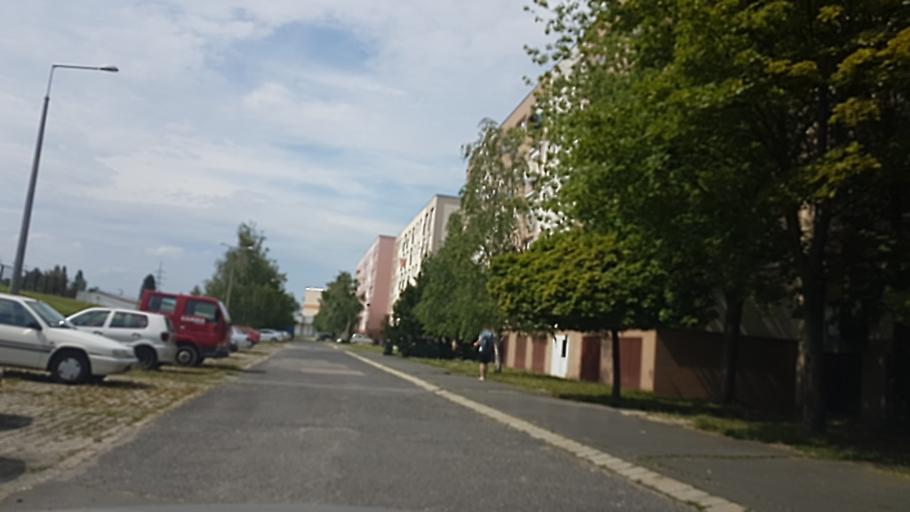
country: HU
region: Gyor-Moson-Sopron
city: Sopron
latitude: 47.6910
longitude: 16.5734
